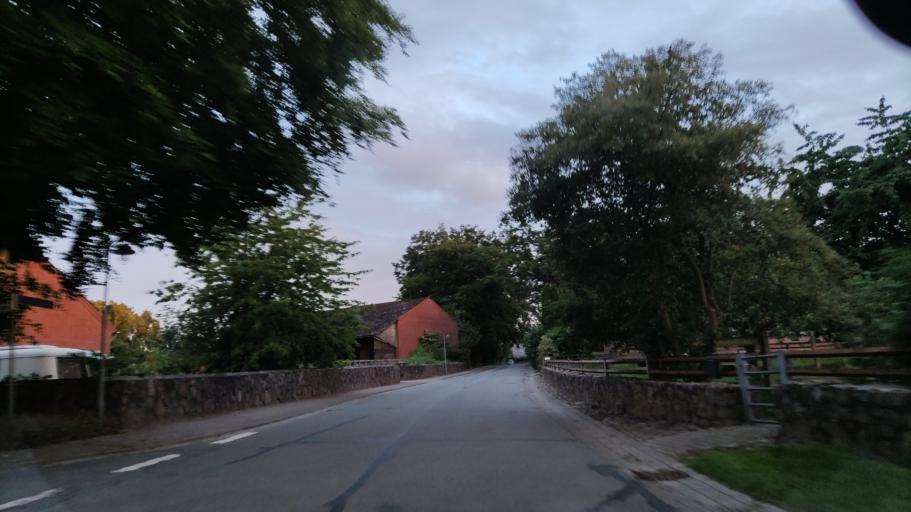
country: DE
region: Lower Saxony
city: Gohrde
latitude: 53.1881
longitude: 10.9306
